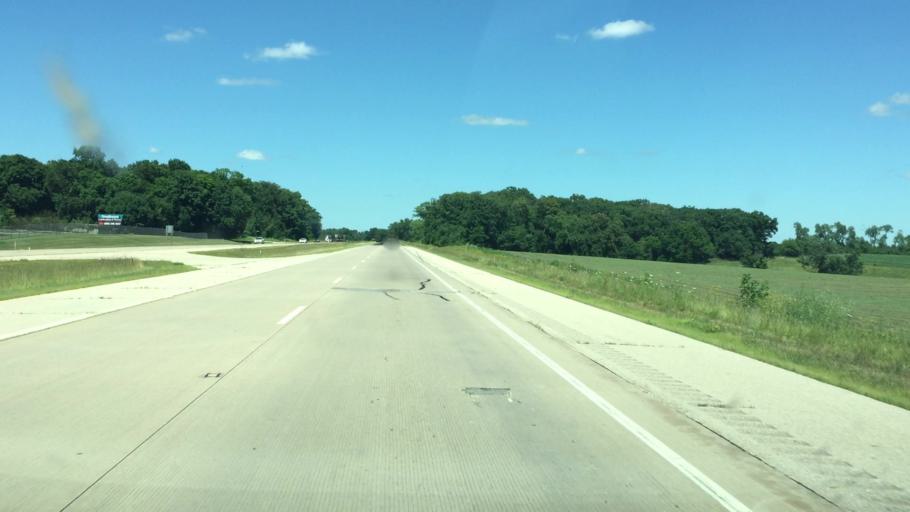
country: US
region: Wisconsin
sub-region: Grant County
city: Platteville
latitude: 42.6867
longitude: -90.5339
